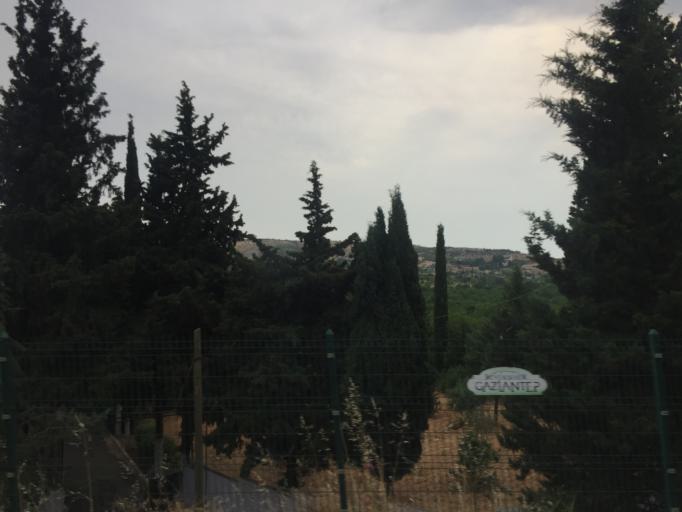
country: TR
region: Gaziantep
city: Gaziantep
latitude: 37.0064
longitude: 37.4320
